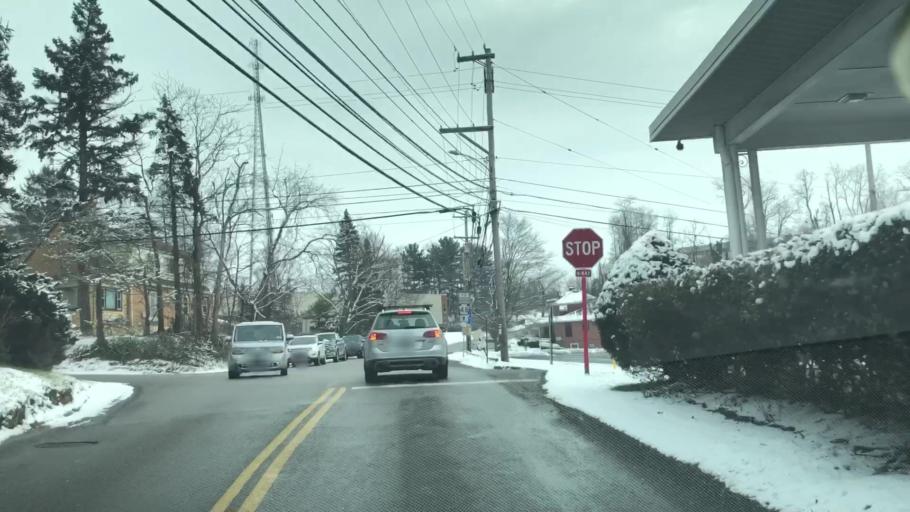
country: US
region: Pennsylvania
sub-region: Allegheny County
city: Monroeville
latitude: 40.4486
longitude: -79.7615
